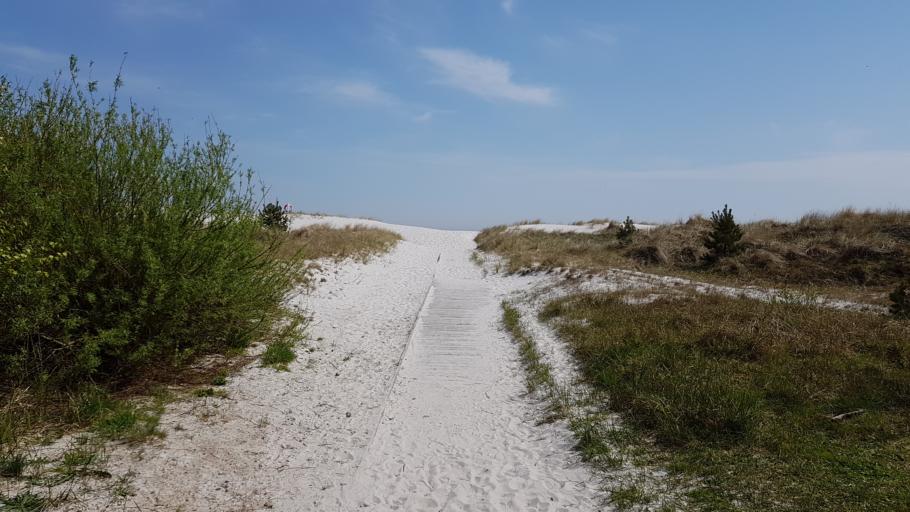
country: DK
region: Capital Region
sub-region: Bornholm Kommune
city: Nexo
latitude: 54.9948
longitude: 15.0880
